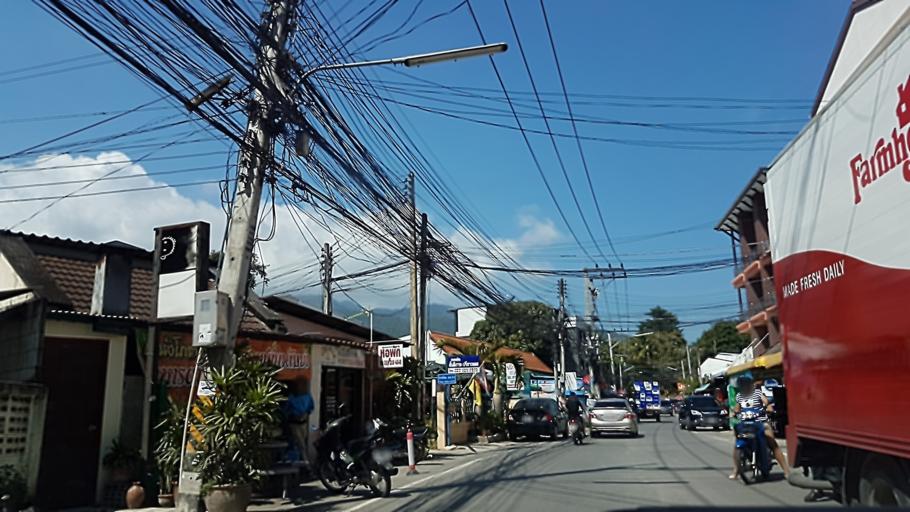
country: TH
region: Chiang Mai
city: Chiang Mai
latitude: 18.8131
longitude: 98.9573
